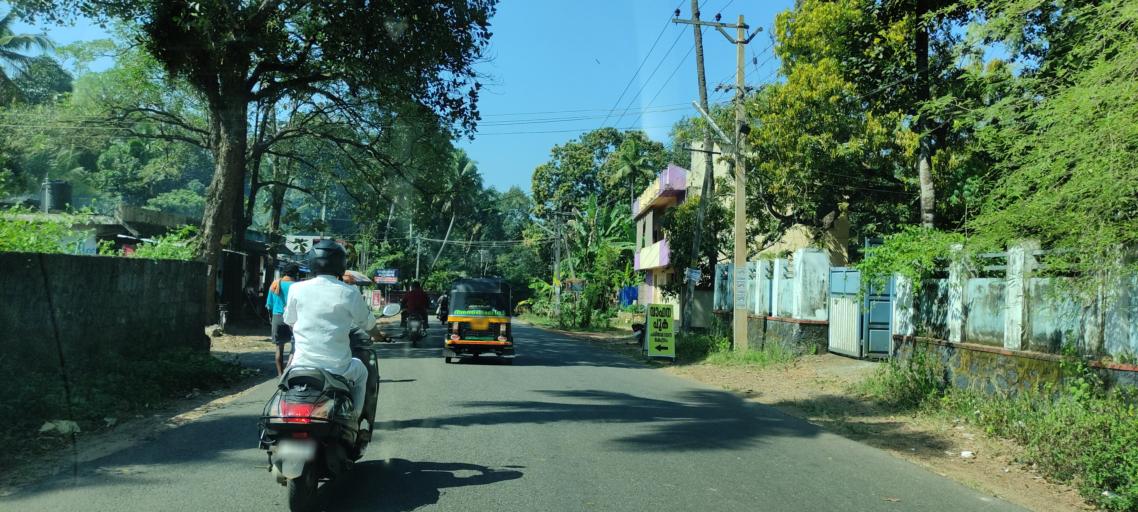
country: IN
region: Kerala
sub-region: Kollam
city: Panmana
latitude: 9.0478
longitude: 76.5729
